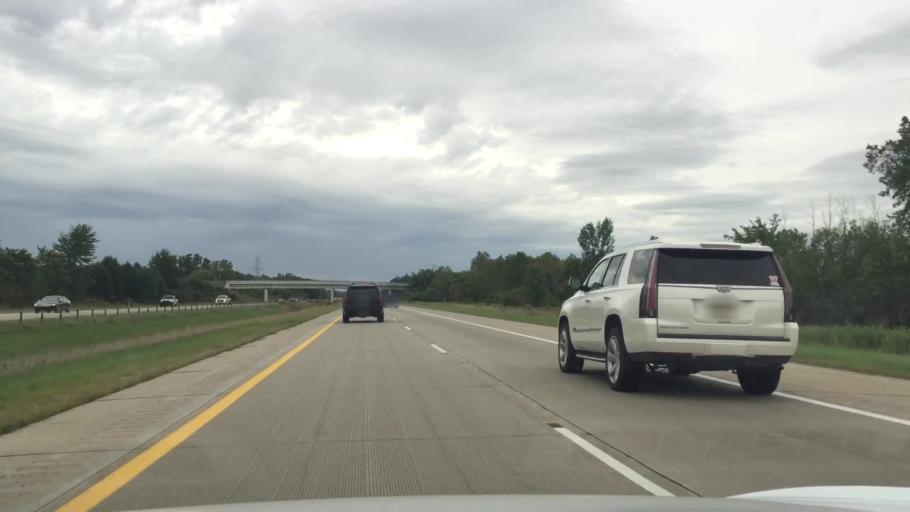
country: US
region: Michigan
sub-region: Macomb County
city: Richmond
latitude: 42.7536
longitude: -82.7058
